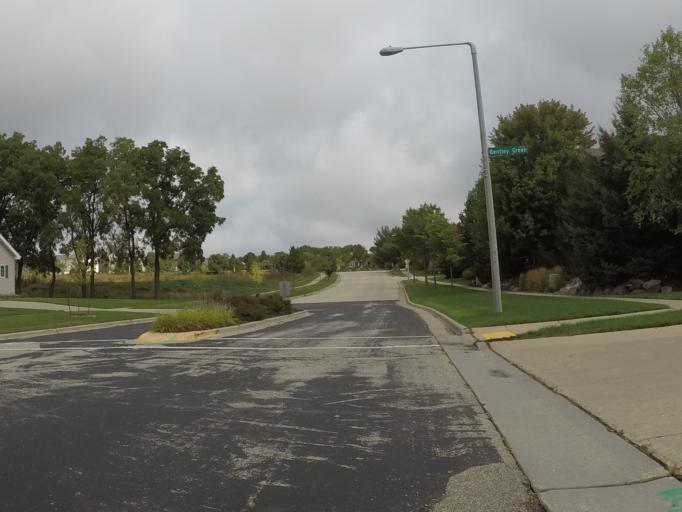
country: US
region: Wisconsin
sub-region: Dane County
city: Verona
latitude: 43.0415
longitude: -89.5422
